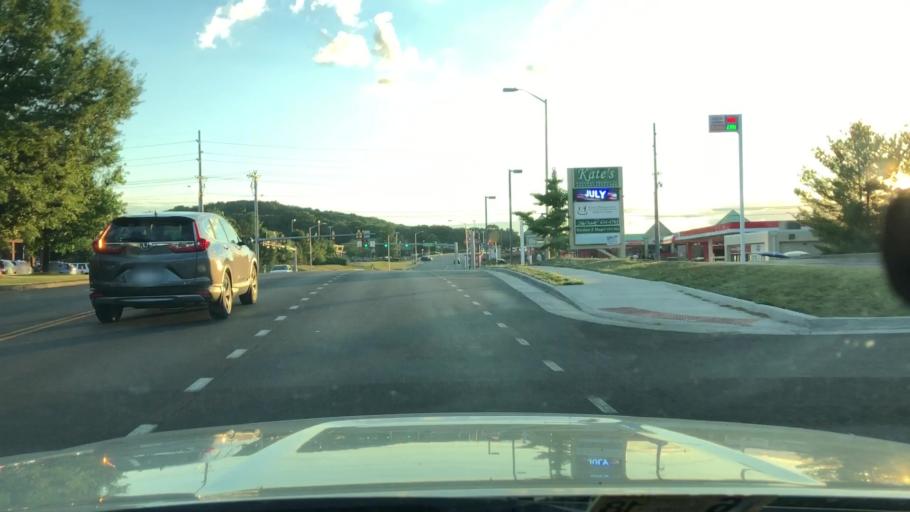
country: US
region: Virginia
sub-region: City of Harrisonburg
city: Harrisonburg
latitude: 38.4292
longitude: -78.8542
